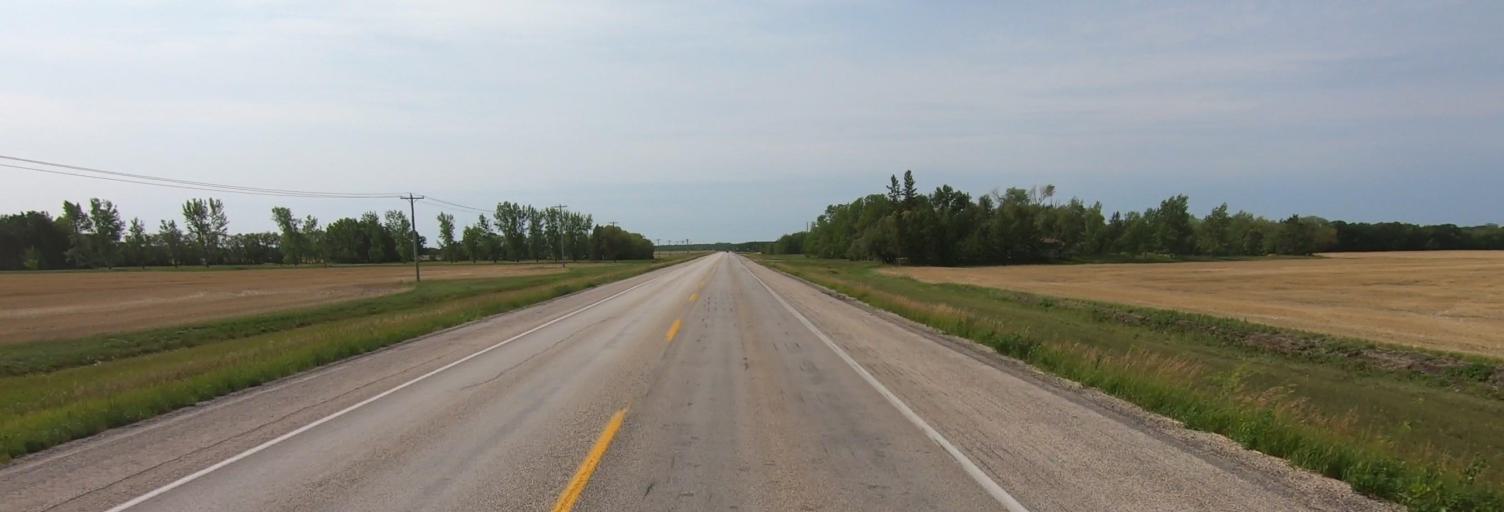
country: CA
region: Manitoba
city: Niverville
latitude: 49.6115
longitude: -97.1251
